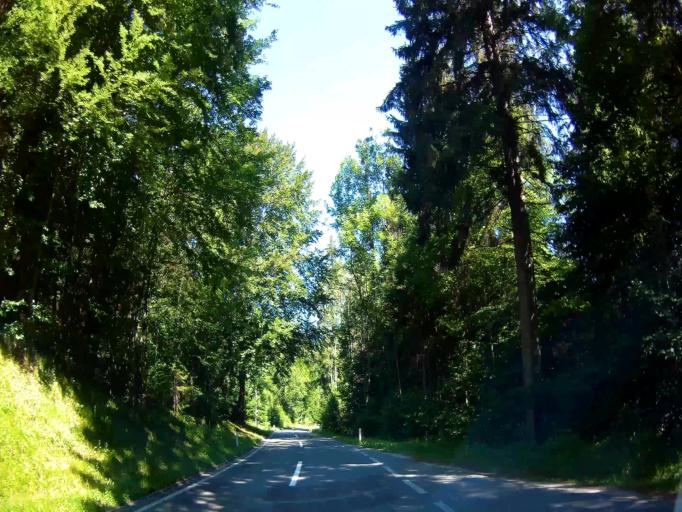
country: AT
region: Carinthia
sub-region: Politischer Bezirk Klagenfurt Land
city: Grafenstein
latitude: 46.5973
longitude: 14.4337
